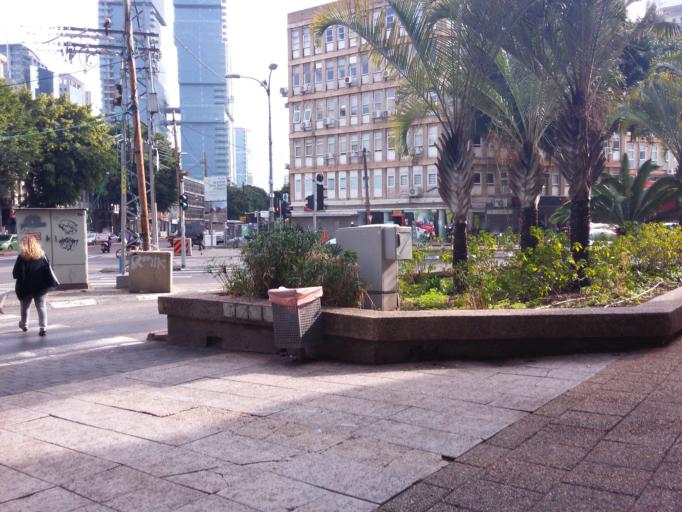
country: IL
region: Tel Aviv
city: Tel Aviv
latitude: 32.0697
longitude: 34.7826
